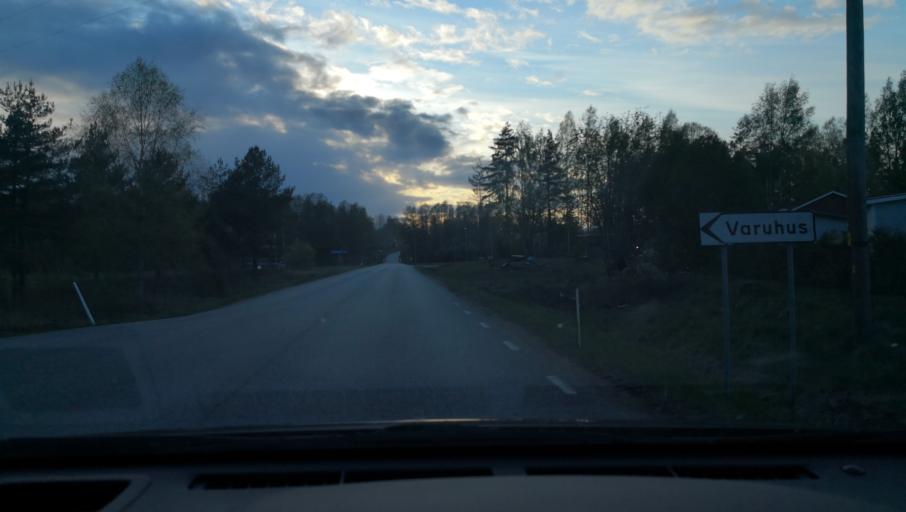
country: SE
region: OErebro
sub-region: Askersunds Kommun
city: Asbro
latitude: 58.9240
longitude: 15.0422
